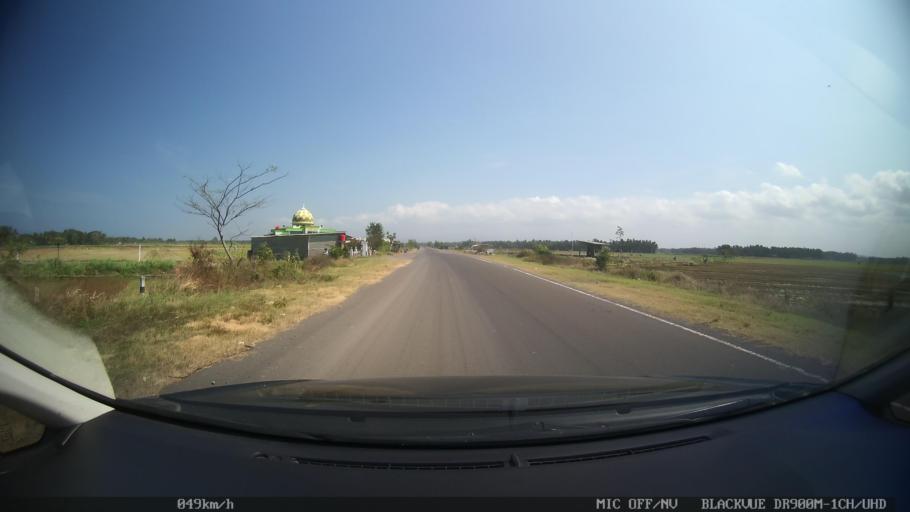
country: ID
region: Daerah Istimewa Yogyakarta
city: Srandakan
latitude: -7.9705
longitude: 110.2089
